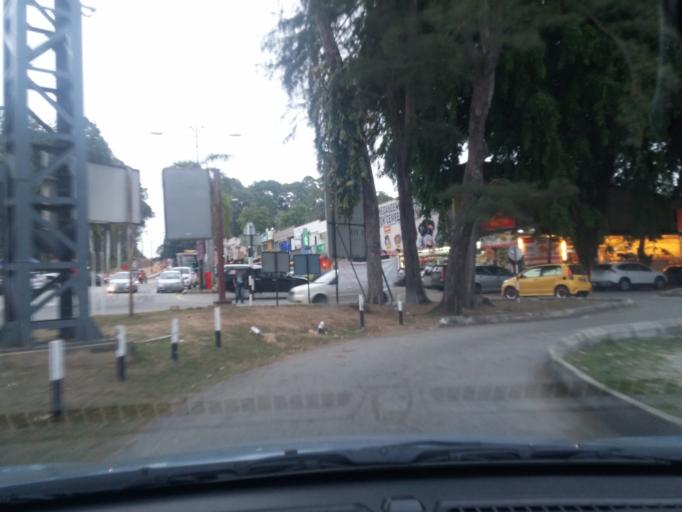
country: MY
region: Pahang
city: Kuantan
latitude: 3.8123
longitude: 103.3713
